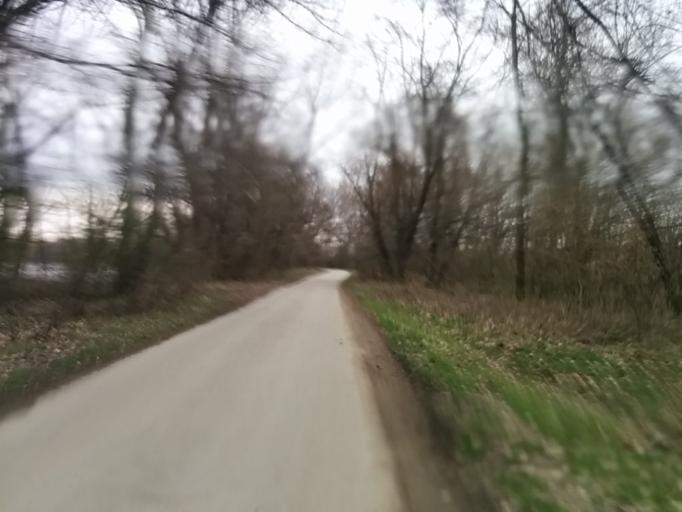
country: SK
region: Trnavsky
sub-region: Okres Galanta
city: Galanta
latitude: 48.2335
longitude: 17.8162
